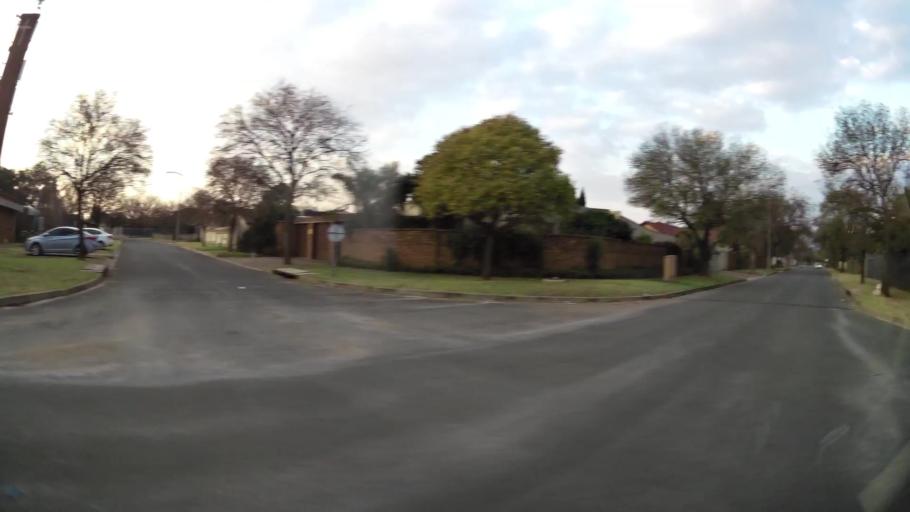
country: ZA
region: Gauteng
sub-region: Ekurhuleni Metropolitan Municipality
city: Benoni
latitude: -26.1718
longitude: 28.3004
